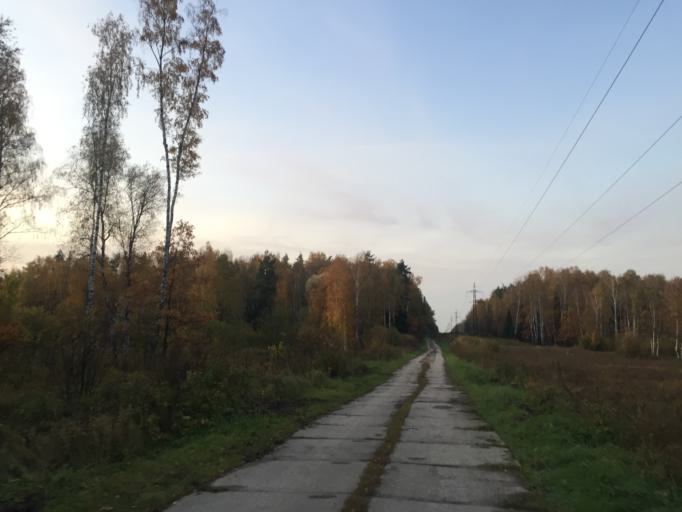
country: RU
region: Moskovskaya
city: Druzhba
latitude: 55.8634
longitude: 37.7681
